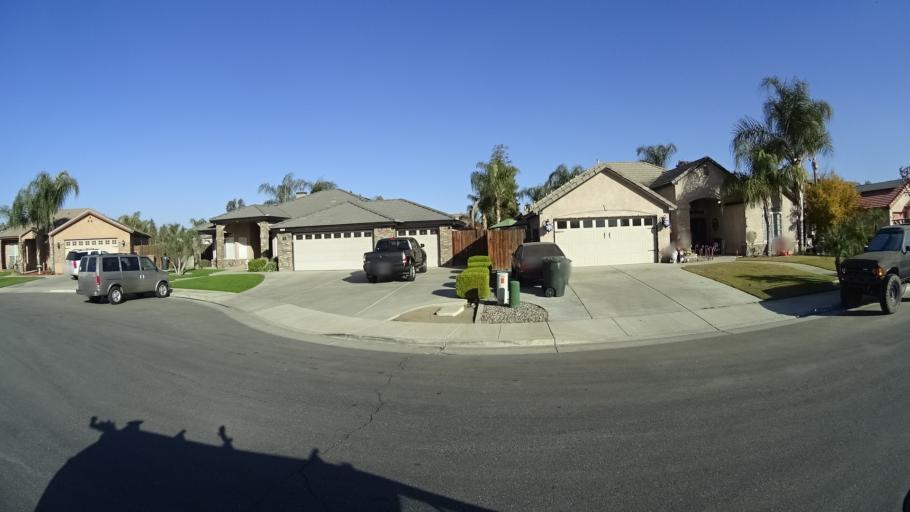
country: US
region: California
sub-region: Kern County
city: Greenfield
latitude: 35.2756
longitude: -119.0381
